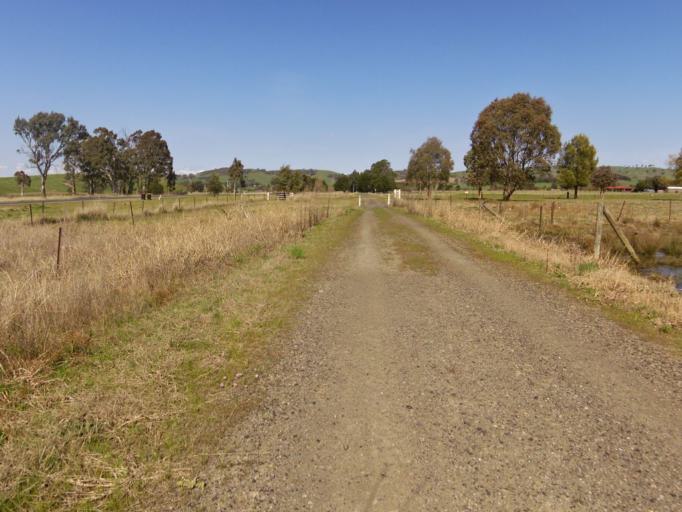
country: AU
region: Victoria
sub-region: Murrindindi
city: Alexandra
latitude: -37.0049
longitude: 145.7491
